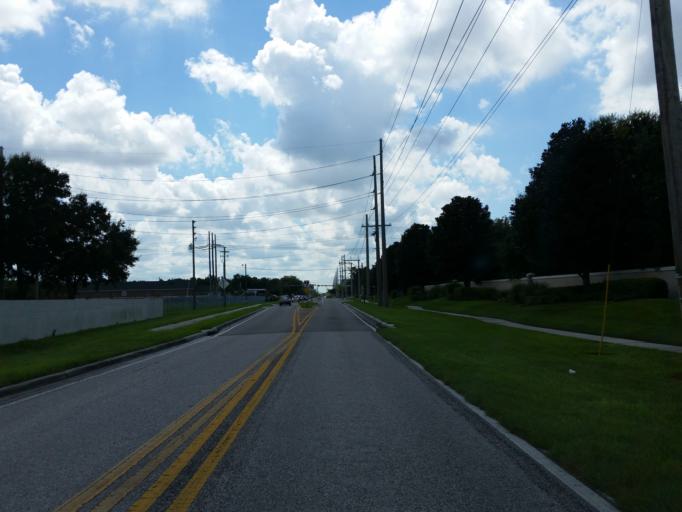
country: US
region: Florida
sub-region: Hillsborough County
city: Riverview
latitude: 27.8569
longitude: -82.3022
